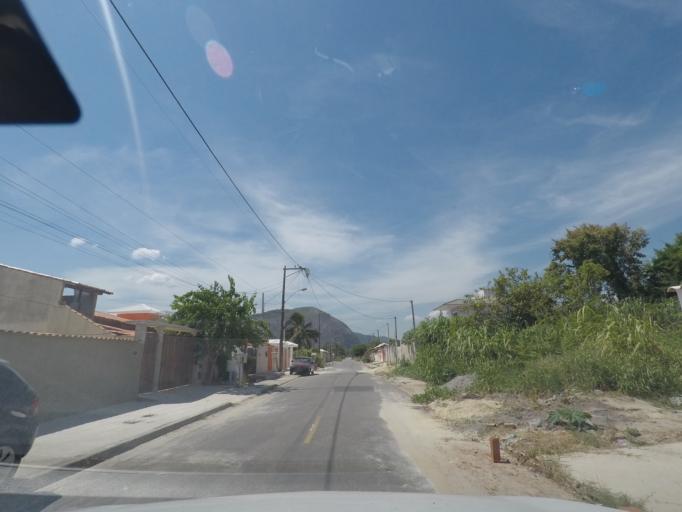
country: BR
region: Rio de Janeiro
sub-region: Marica
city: Marica
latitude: -22.9617
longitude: -42.9586
